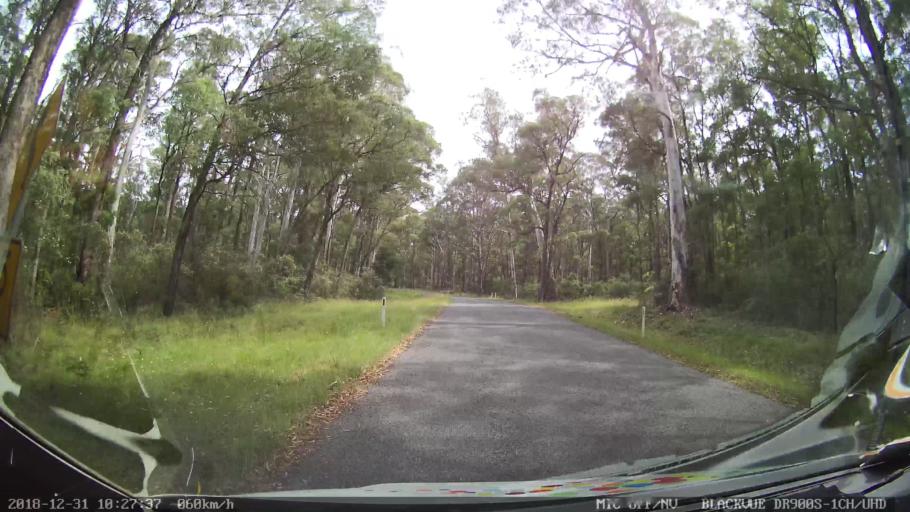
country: AU
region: New South Wales
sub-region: Snowy River
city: Jindabyne
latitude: -36.4853
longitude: 148.1448
